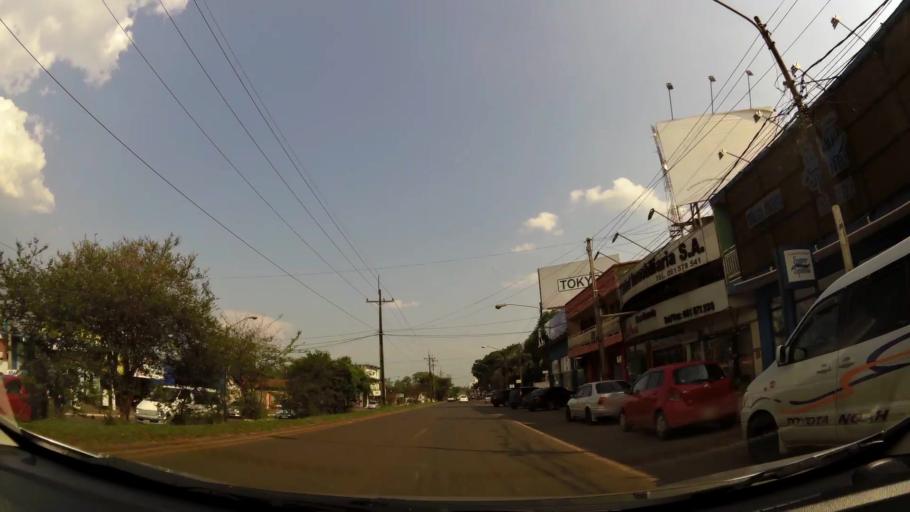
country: PY
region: Alto Parana
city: Presidente Franco
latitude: -25.5184
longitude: -54.6412
